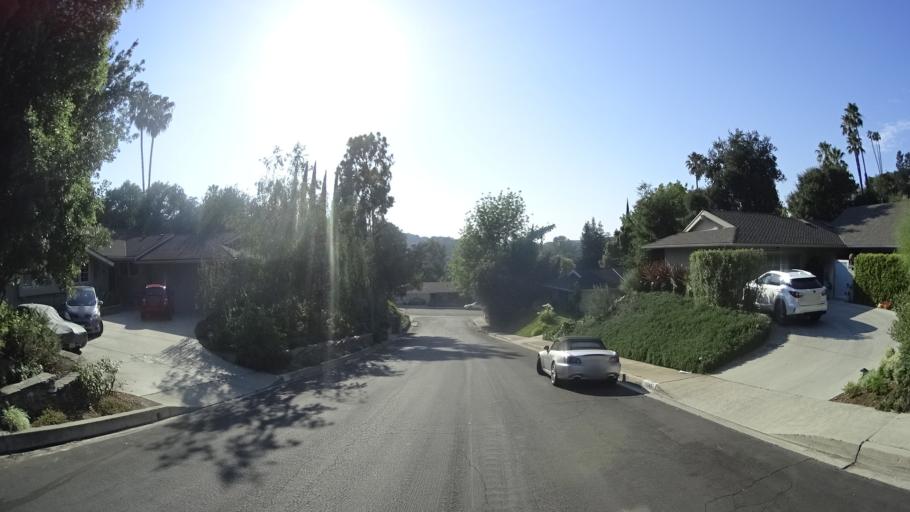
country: US
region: California
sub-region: Los Angeles County
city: Universal City
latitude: 34.1286
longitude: -118.3855
